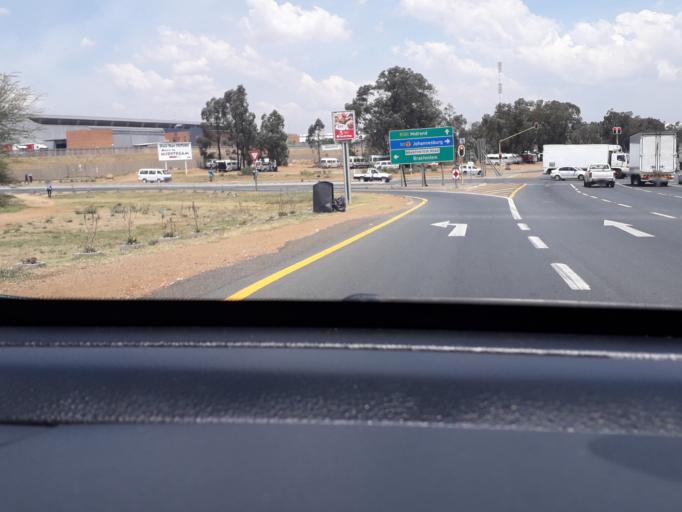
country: ZA
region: Gauteng
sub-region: City of Tshwane Metropolitan Municipality
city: Centurion
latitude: -25.9096
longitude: 28.1595
